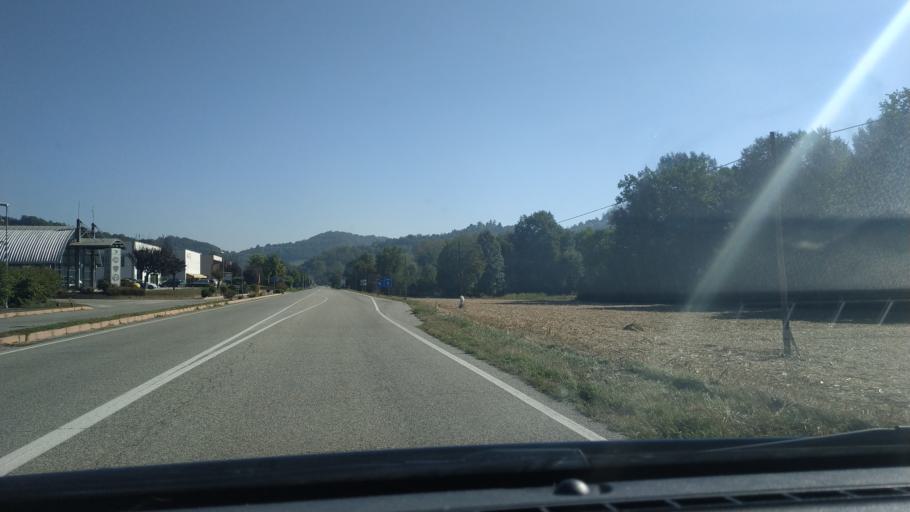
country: IT
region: Piedmont
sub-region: Provincia di Alessandria
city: Murisengo
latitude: 45.0868
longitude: 8.1242
